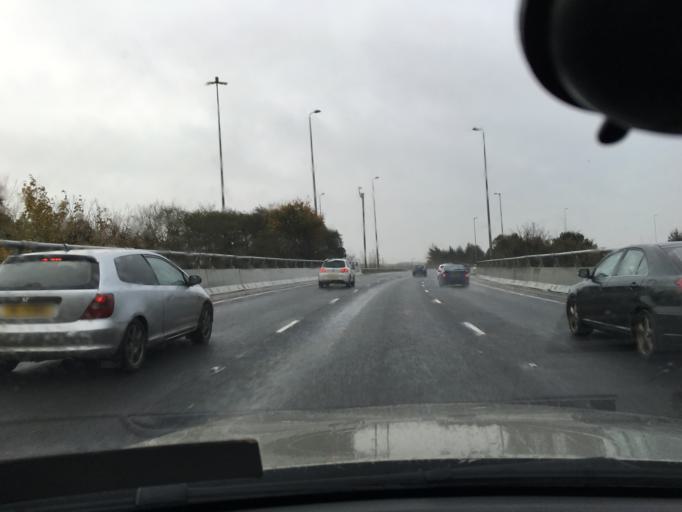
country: GB
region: Northern Ireland
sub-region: Newtownabbey District
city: Newtownabbey
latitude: 54.6471
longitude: -5.9173
